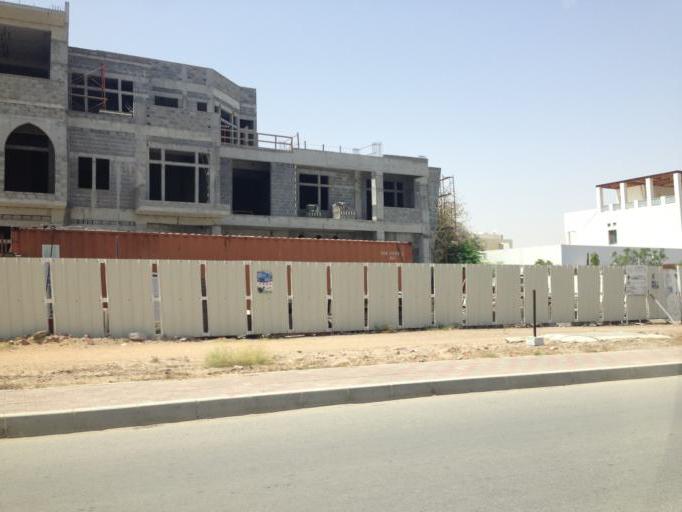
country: OM
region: Muhafazat Masqat
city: Bawshar
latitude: 23.6040
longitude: 58.3575
